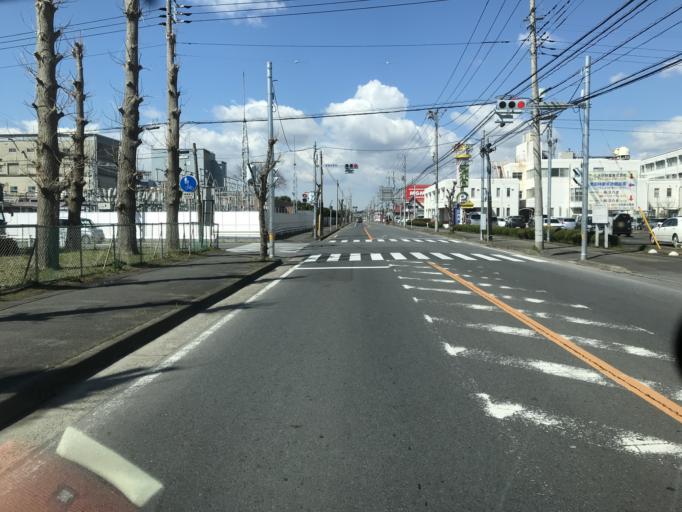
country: JP
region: Ibaraki
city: Ishioka
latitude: 36.1195
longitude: 140.2315
